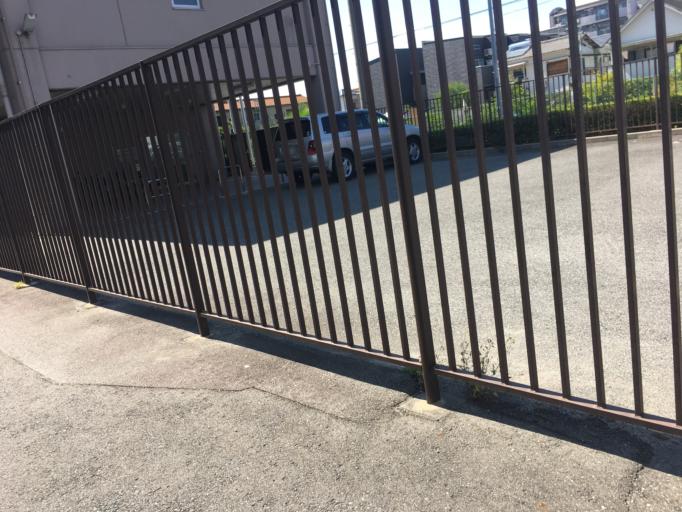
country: JP
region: Osaka
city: Sakai
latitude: 34.5938
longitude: 135.5084
